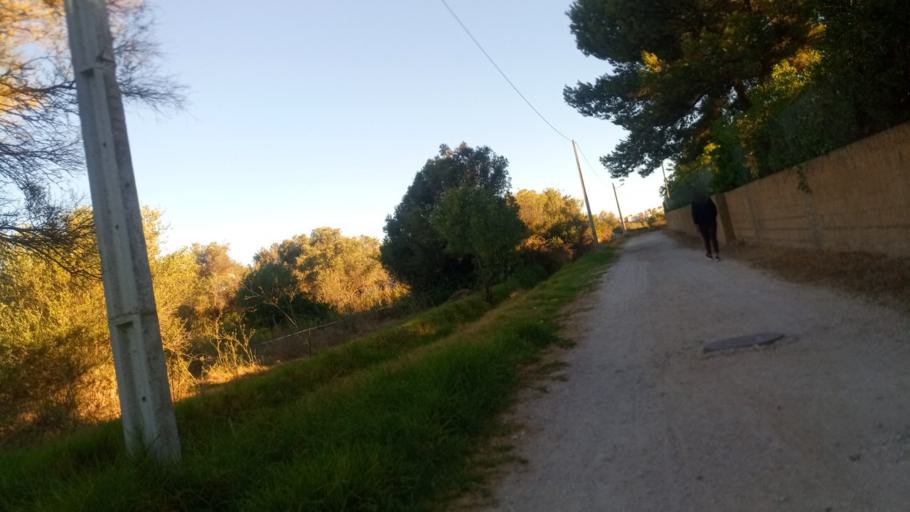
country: PT
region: Faro
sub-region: Tavira
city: Tavira
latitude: 37.1359
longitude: -7.6042
